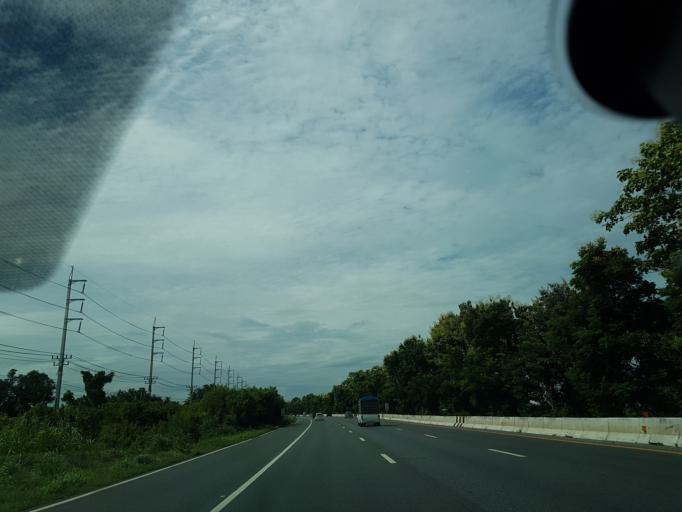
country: TH
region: Ang Thong
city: Chaiyo
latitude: 14.7006
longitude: 100.4562
